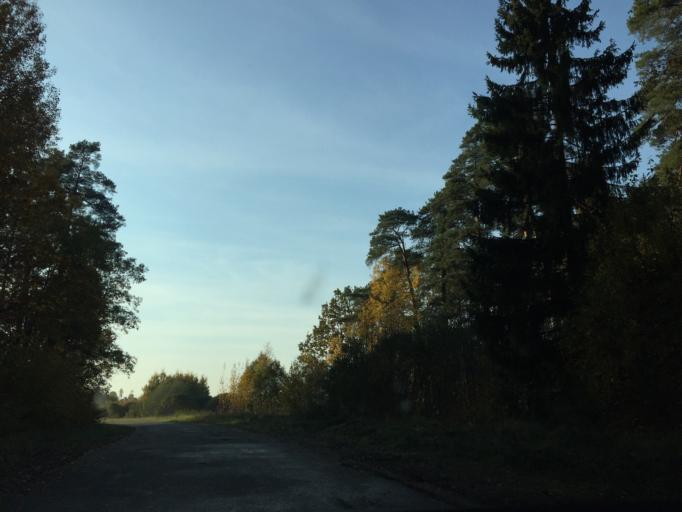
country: LV
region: Skrunda
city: Skrunda
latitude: 56.6804
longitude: 22.1431
